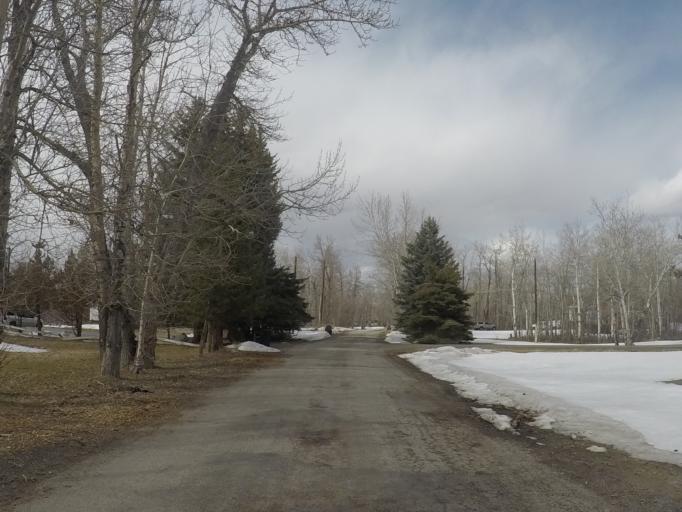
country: US
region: Montana
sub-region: Carbon County
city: Red Lodge
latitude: 45.1739
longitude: -109.2479
